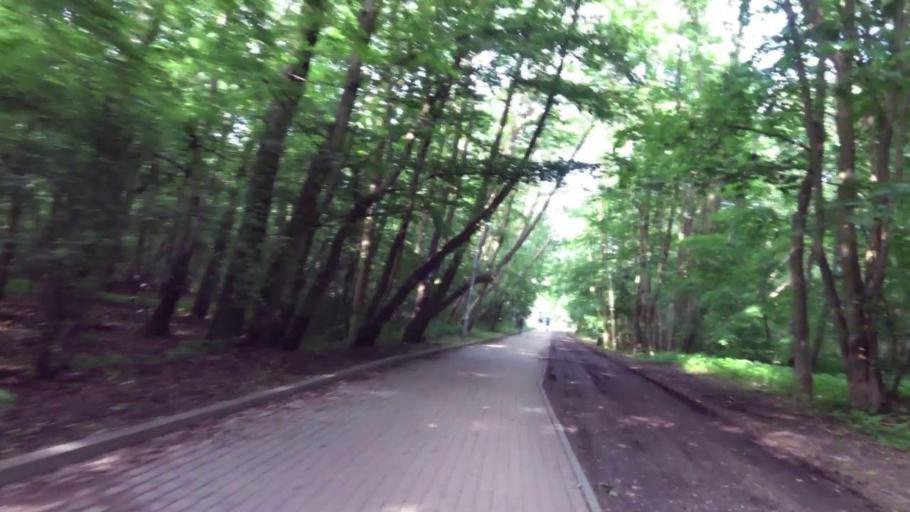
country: PL
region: West Pomeranian Voivodeship
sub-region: Powiat kolobrzeski
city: Kolobrzeg
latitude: 54.1747
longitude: 15.5348
